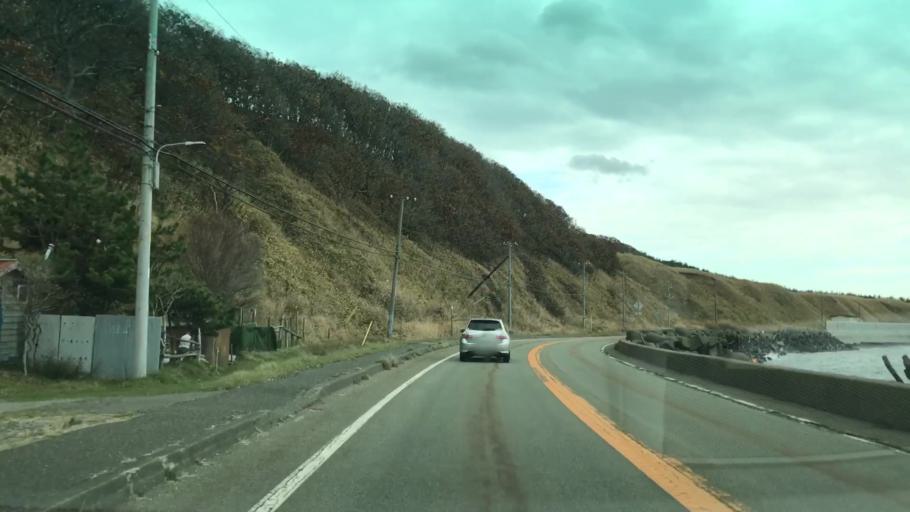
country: JP
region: Hokkaido
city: Shizunai-furukawacho
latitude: 42.0509
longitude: 143.0928
